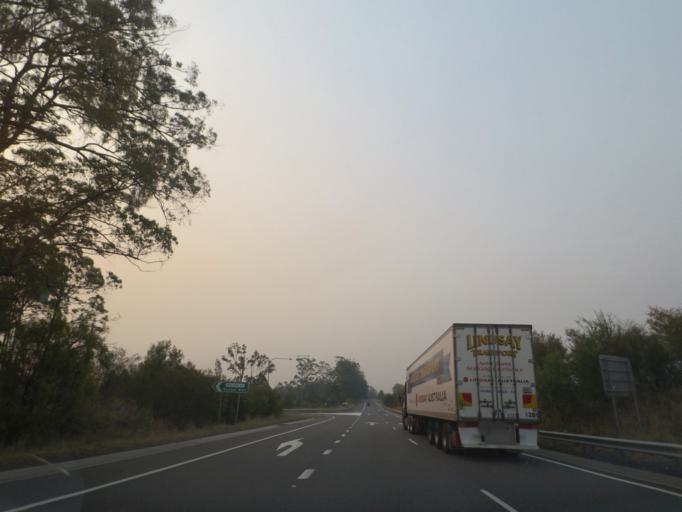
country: AU
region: New South Wales
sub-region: Nambucca Shire
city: Macksville
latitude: -30.8429
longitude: 152.9042
